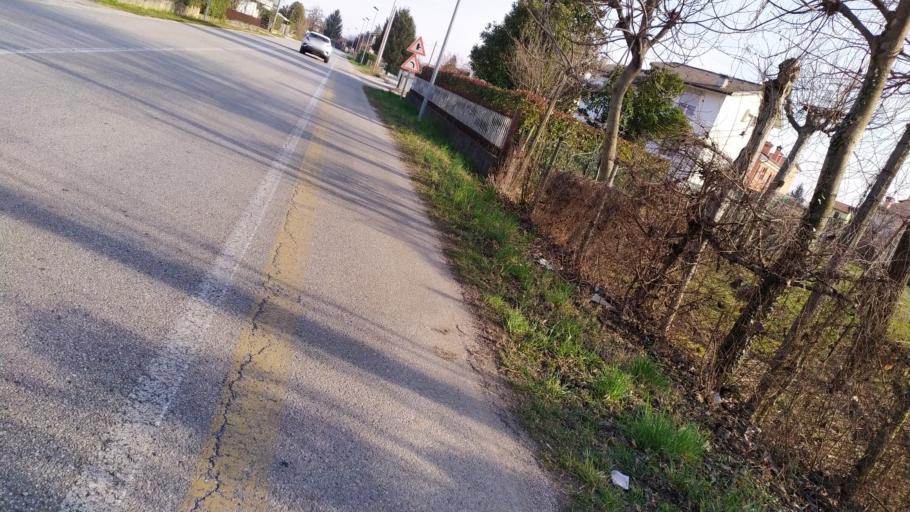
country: IT
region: Veneto
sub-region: Provincia di Vicenza
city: Marano Vicentino
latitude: 45.6922
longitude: 11.4185
